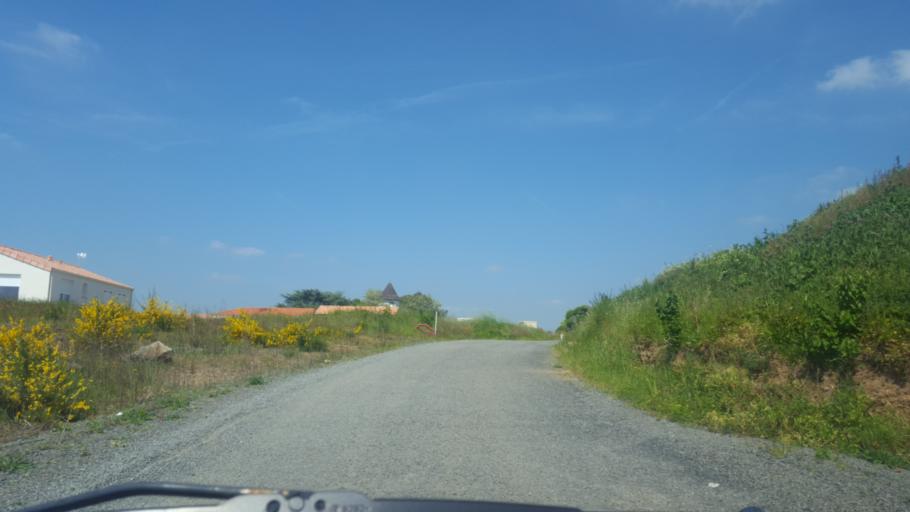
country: FR
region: Pays de la Loire
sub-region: Departement de la Loire-Atlantique
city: La Limouziniere
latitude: 46.9604
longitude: -1.5774
